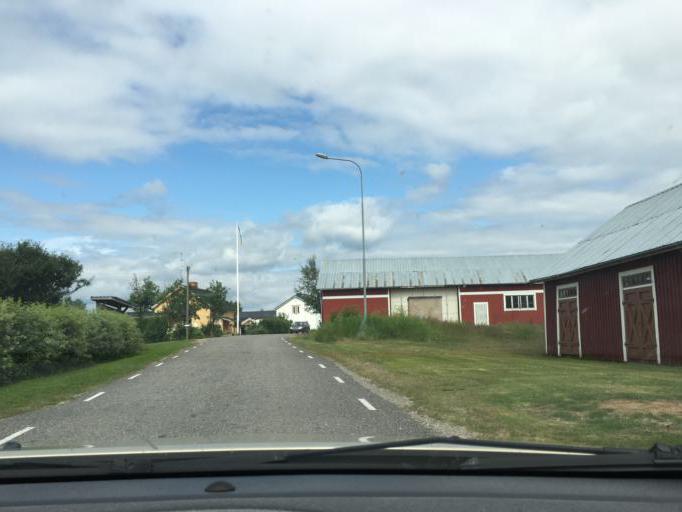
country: SE
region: Norrbotten
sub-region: Overkalix Kommun
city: OEverkalix
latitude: 66.1059
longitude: 22.7827
